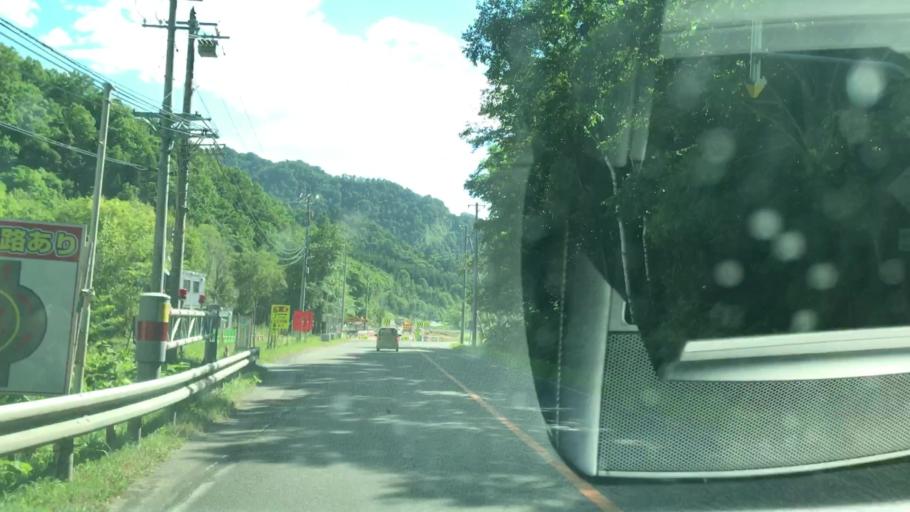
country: JP
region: Hokkaido
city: Shimo-furano
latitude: 42.9130
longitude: 142.5870
